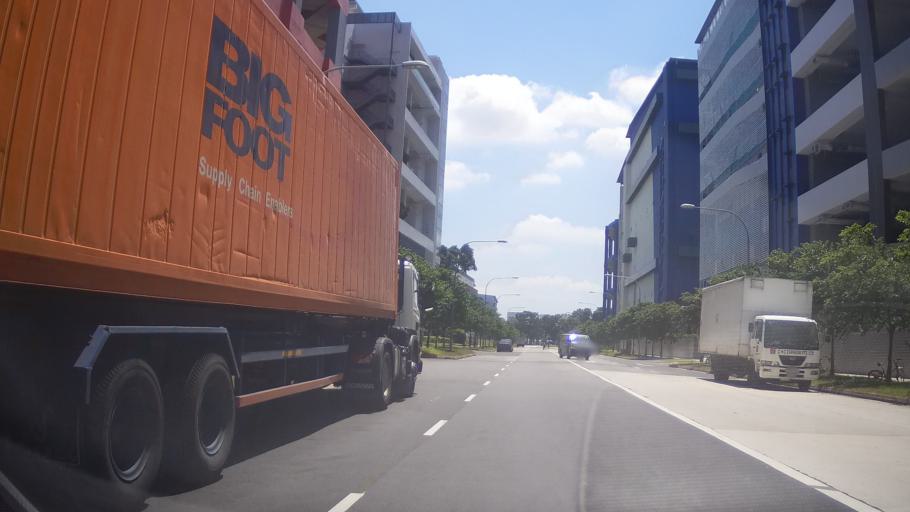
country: SG
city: Singapore
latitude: 1.3155
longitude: 103.7221
